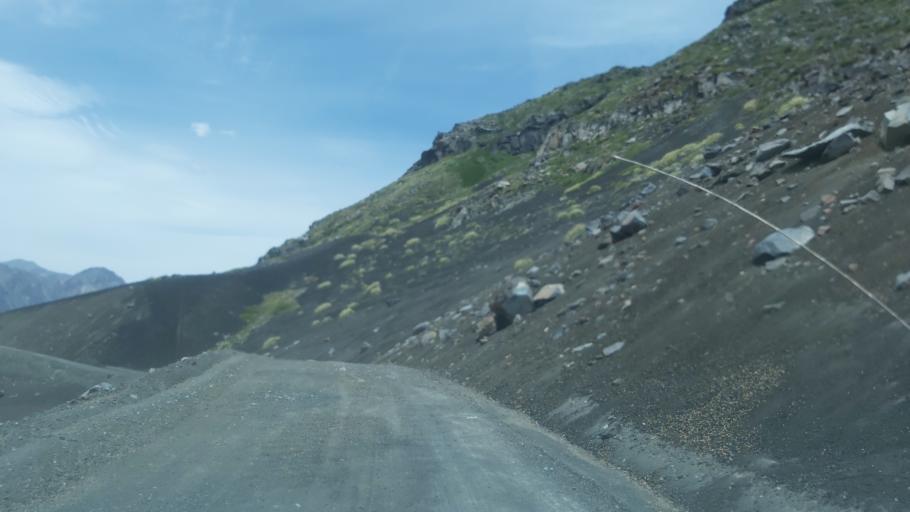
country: AR
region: Neuquen
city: Andacollo
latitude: -37.4086
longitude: -71.2972
